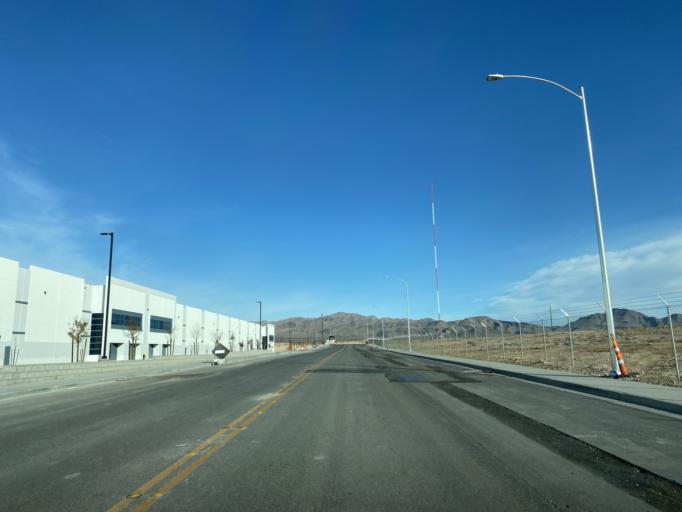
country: US
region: Nevada
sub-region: Clark County
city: Nellis Air Force Base
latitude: 36.2670
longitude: -115.0477
